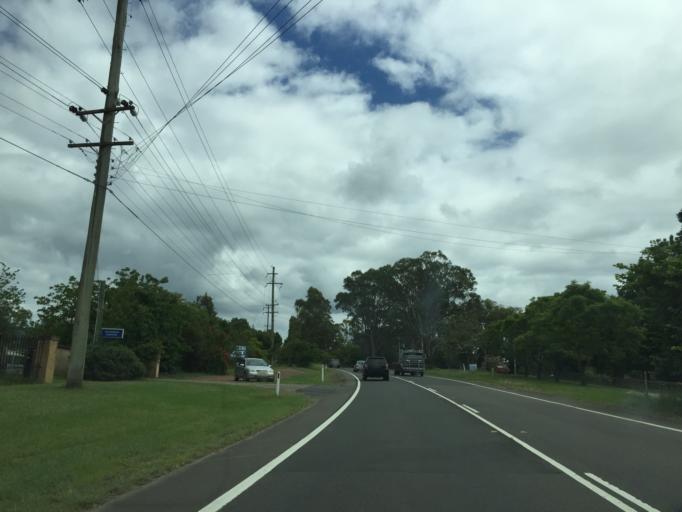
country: AU
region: New South Wales
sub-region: Hawkesbury
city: Richmond
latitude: -33.5589
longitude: 150.7015
